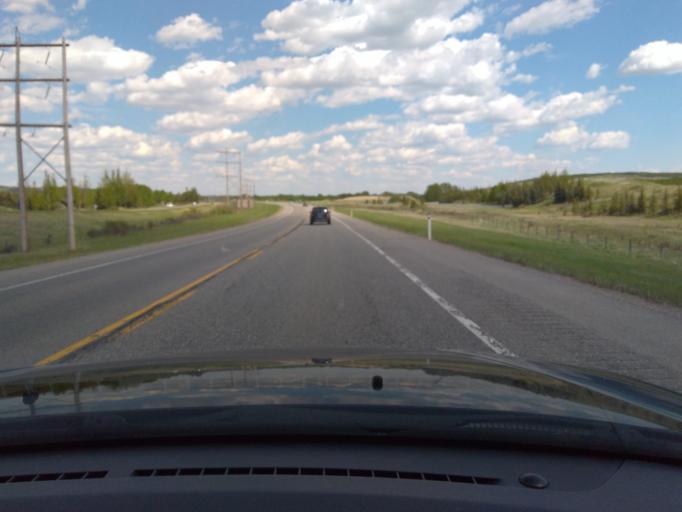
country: CA
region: Alberta
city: Calgary
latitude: 51.0172
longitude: -114.2730
